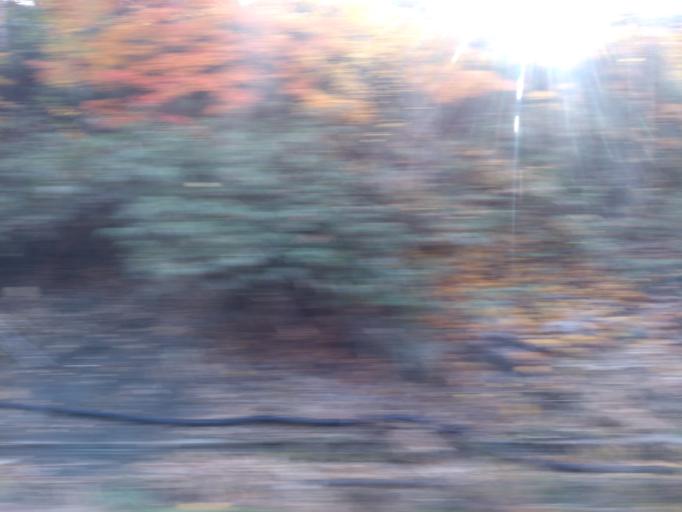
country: JP
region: Hokkaido
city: Kitahiroshima
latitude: 43.0001
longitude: 141.5220
